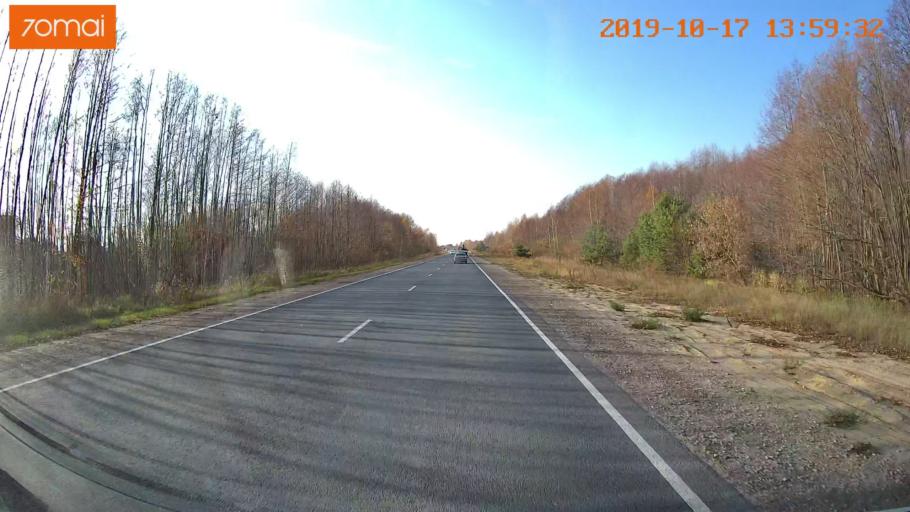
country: RU
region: Rjazan
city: Spas-Klepiki
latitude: 55.1430
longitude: 40.2002
